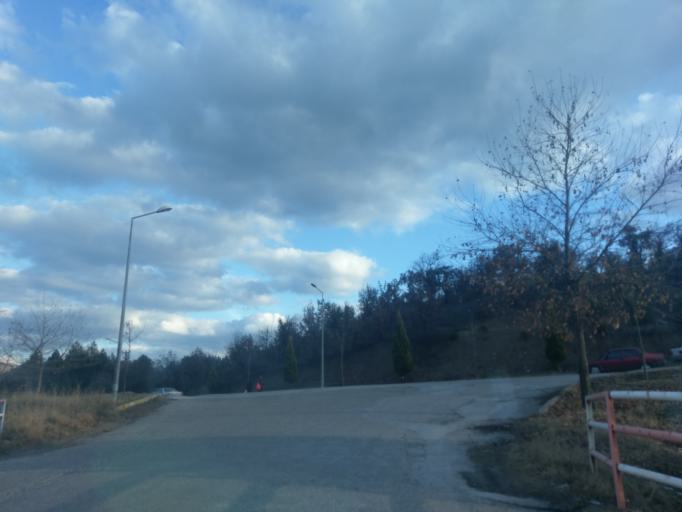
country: TR
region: Kuetahya
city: Gediz
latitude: 38.9881
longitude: 29.3869
